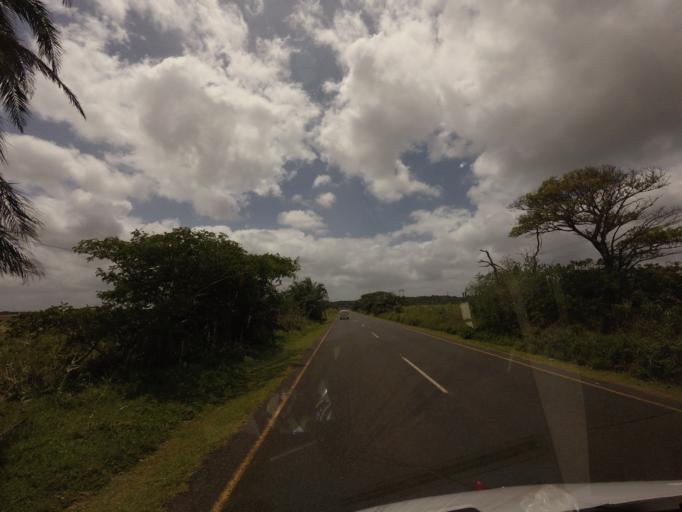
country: ZA
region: KwaZulu-Natal
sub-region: uMkhanyakude District Municipality
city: Mtubatuba
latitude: -28.3714
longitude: 32.4031
